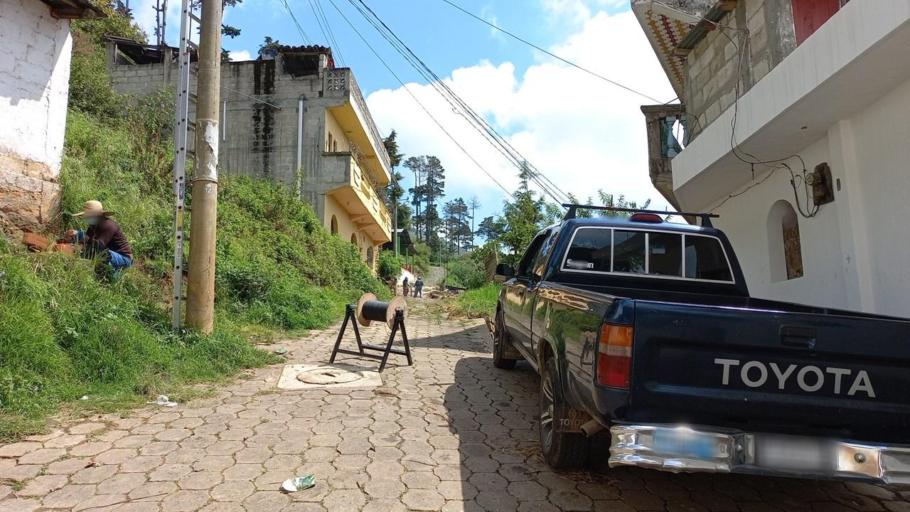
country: GT
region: Totonicapan
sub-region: Municipio de San Andres Xecul
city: San Andres Xecul
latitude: 14.9070
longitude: -91.4847
